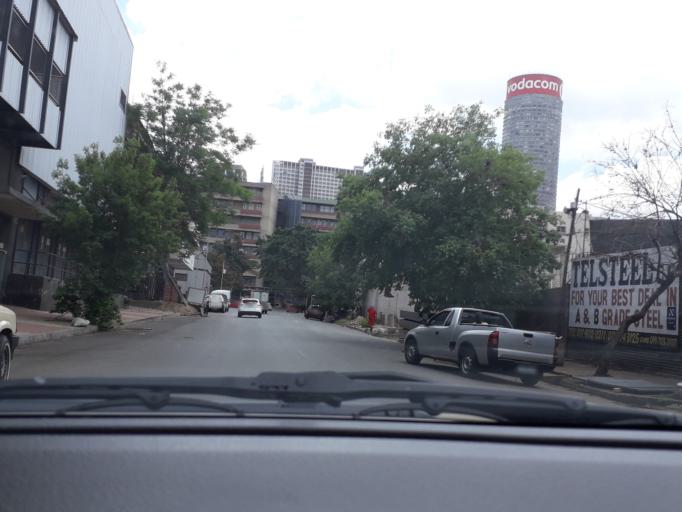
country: ZA
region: Gauteng
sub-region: City of Johannesburg Metropolitan Municipality
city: Johannesburg
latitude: -26.1957
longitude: 28.0563
